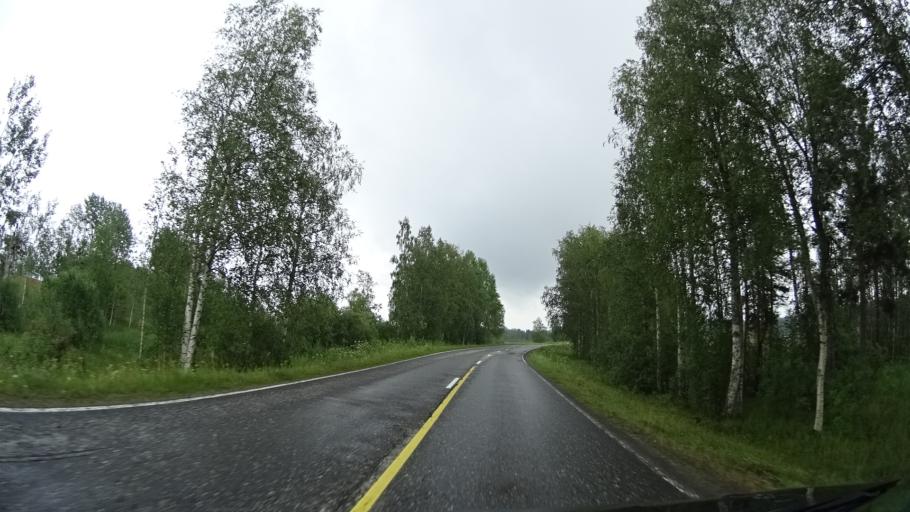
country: FI
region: North Karelia
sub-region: Keski-Karjala
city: Raeaekkylae
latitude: 62.3090
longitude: 29.5317
